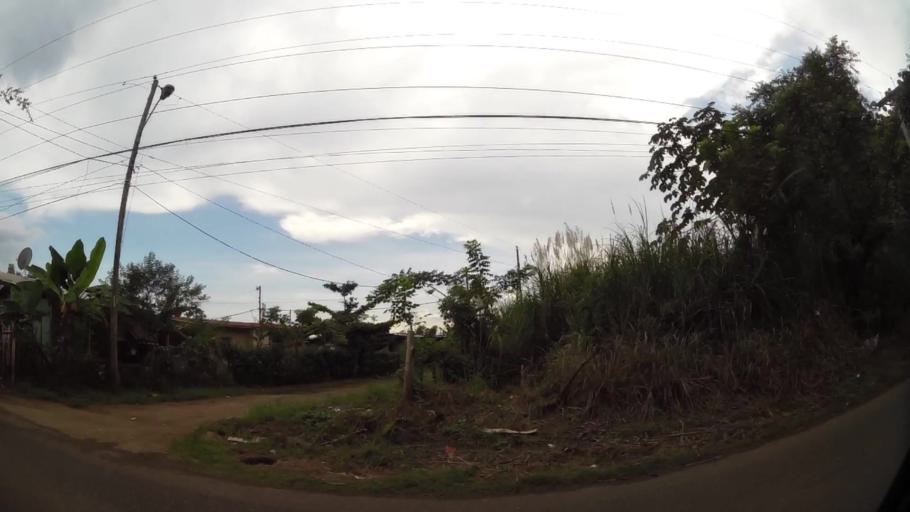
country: PA
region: Panama
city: Cabra Numero Uno
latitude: 9.1207
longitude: -79.3581
